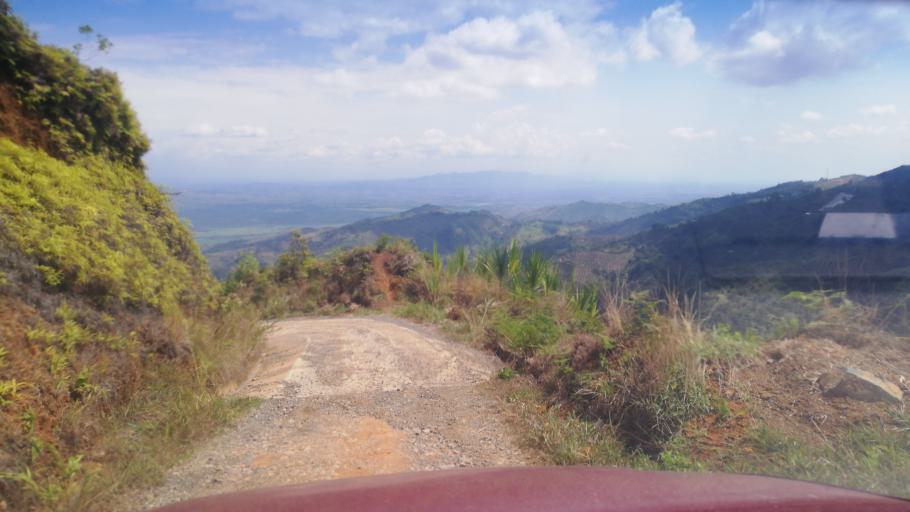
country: CO
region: Risaralda
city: Balboa
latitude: 4.9288
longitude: -75.9635
